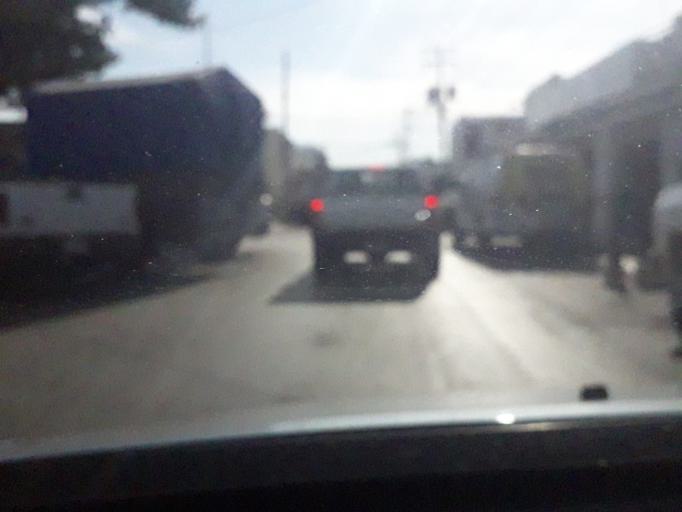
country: MX
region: Yucatan
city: Merida
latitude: 20.9617
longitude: -89.6164
